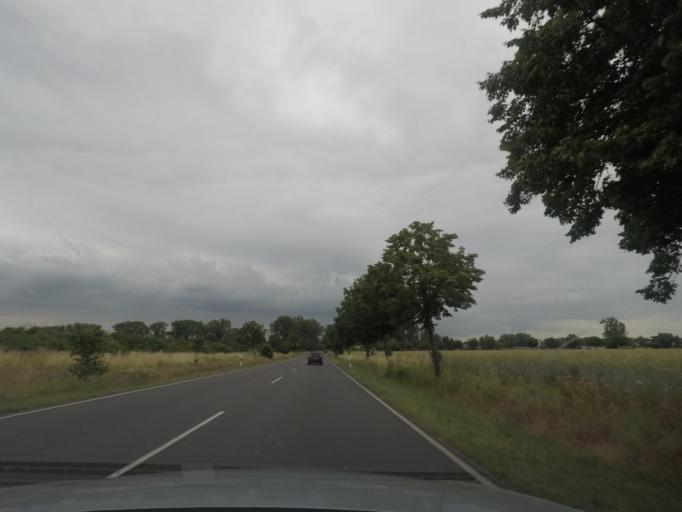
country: DE
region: Saxony-Anhalt
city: Haldensleben I
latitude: 52.2900
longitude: 11.4340
